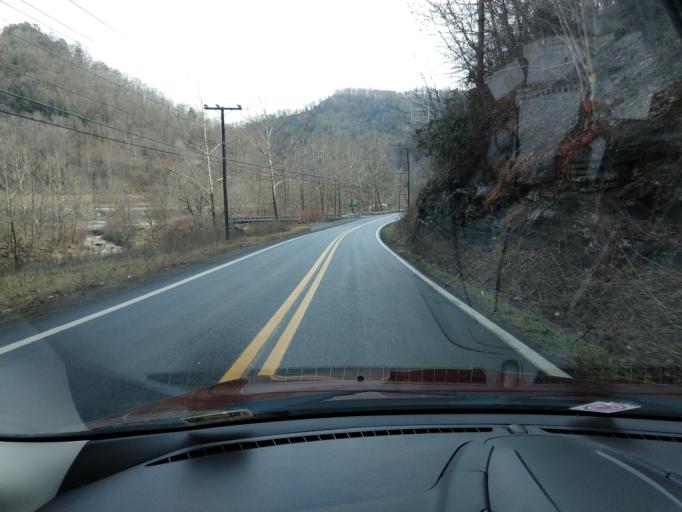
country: US
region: West Virginia
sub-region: McDowell County
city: Welch
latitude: 37.3393
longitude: -81.7365
